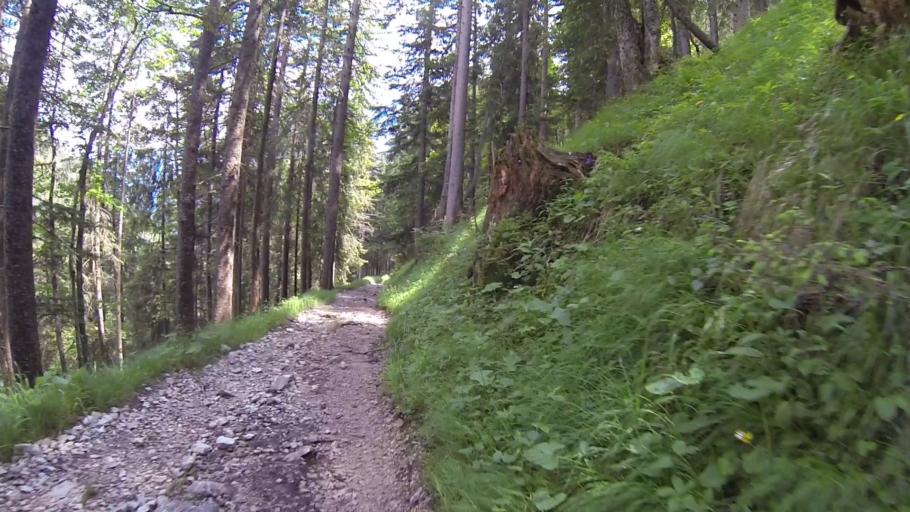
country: DE
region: Bavaria
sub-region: Swabia
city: Halblech
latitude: 47.5300
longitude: 10.8335
